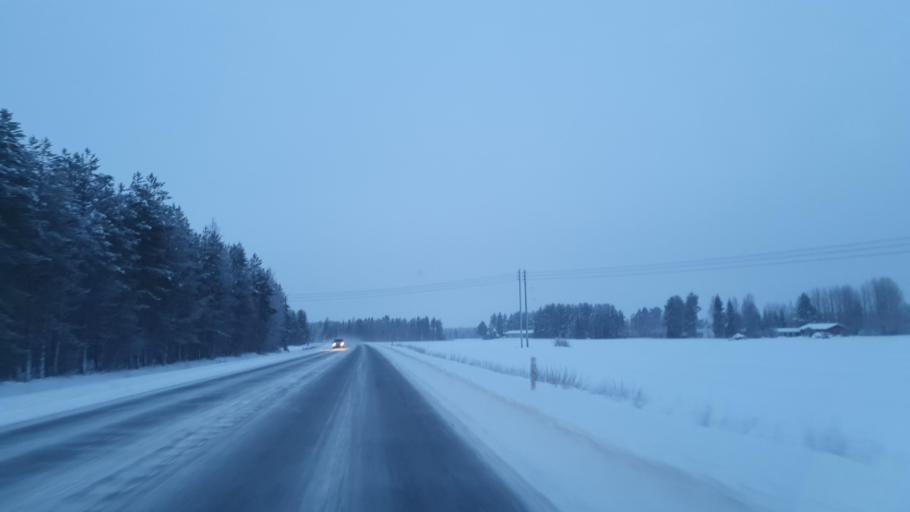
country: FI
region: Northern Ostrobothnia
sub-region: Oulunkaari
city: Utajaervi
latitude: 64.7137
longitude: 26.5142
